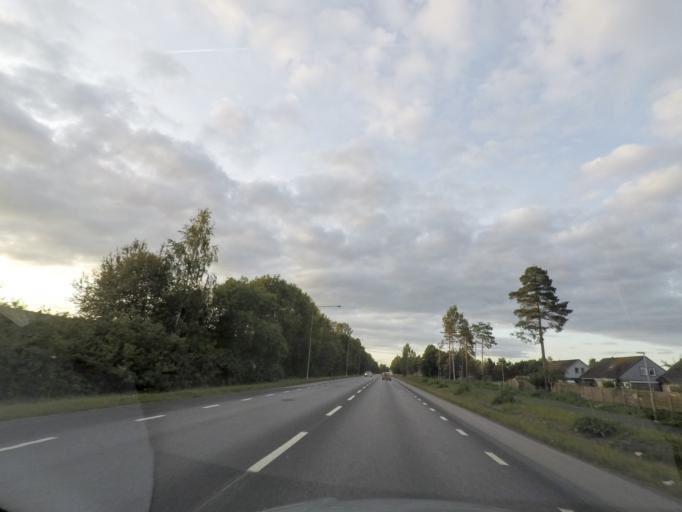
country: SE
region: OErebro
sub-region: Hallefors Kommun
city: Haellefors
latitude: 59.7709
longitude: 14.5234
